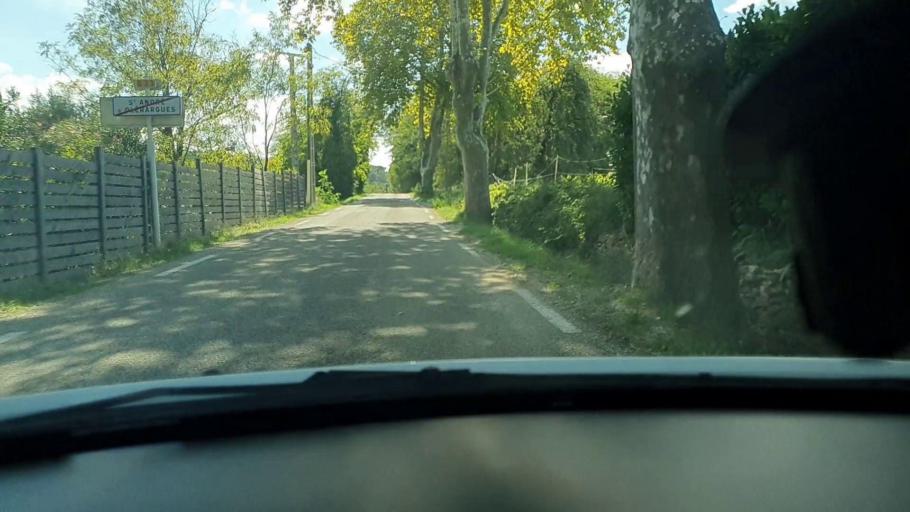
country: FR
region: Languedoc-Roussillon
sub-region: Departement du Gard
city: Goudargues
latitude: 44.1606
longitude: 4.4864
